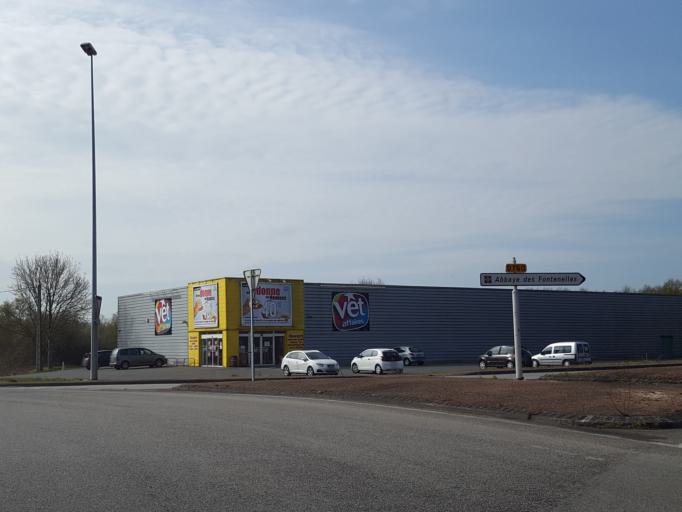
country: FR
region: Pays de la Loire
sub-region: Departement de la Vendee
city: La Roche-sur-Yon
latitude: 46.6621
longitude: -1.4626
